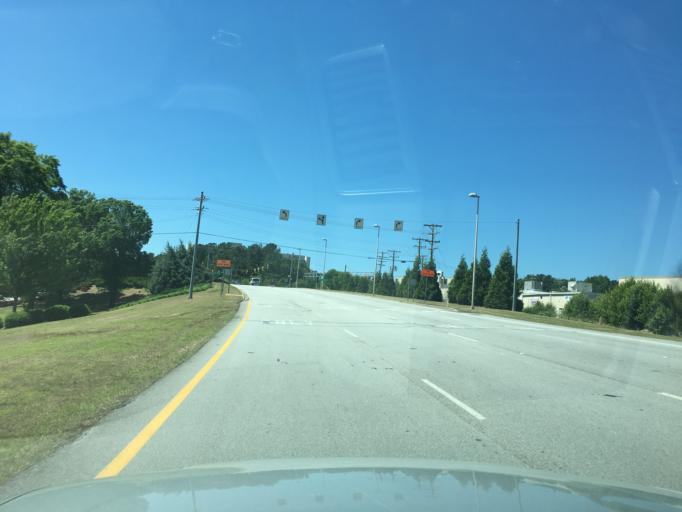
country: US
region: South Carolina
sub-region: Greenville County
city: Wade Hampton
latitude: 34.8543
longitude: -82.3334
